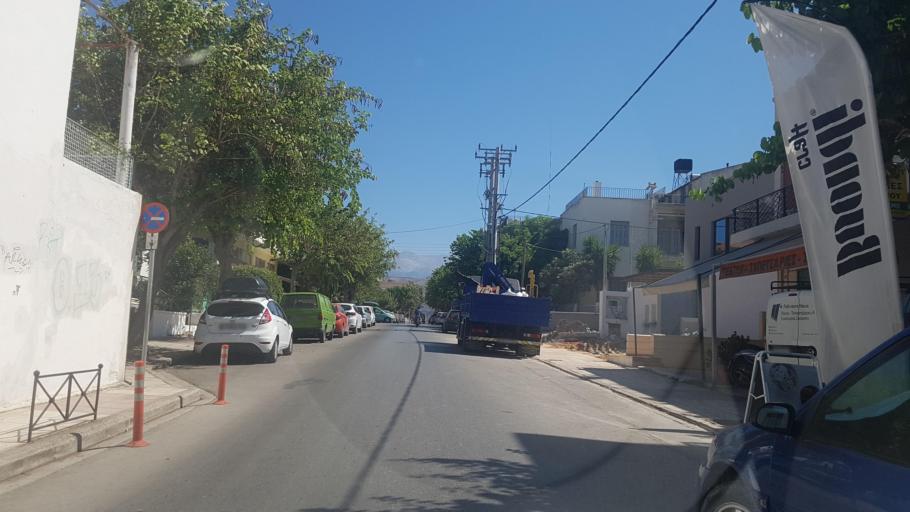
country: GR
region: Crete
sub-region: Nomos Chanias
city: Chania
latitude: 35.5094
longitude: 24.0175
